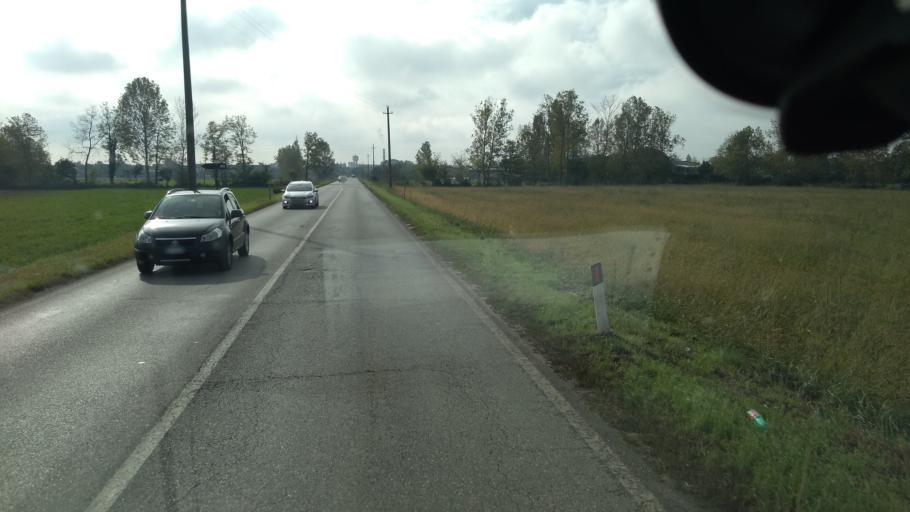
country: IT
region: Lombardy
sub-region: Provincia di Bergamo
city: Vidalengo
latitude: 45.5302
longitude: 9.6389
